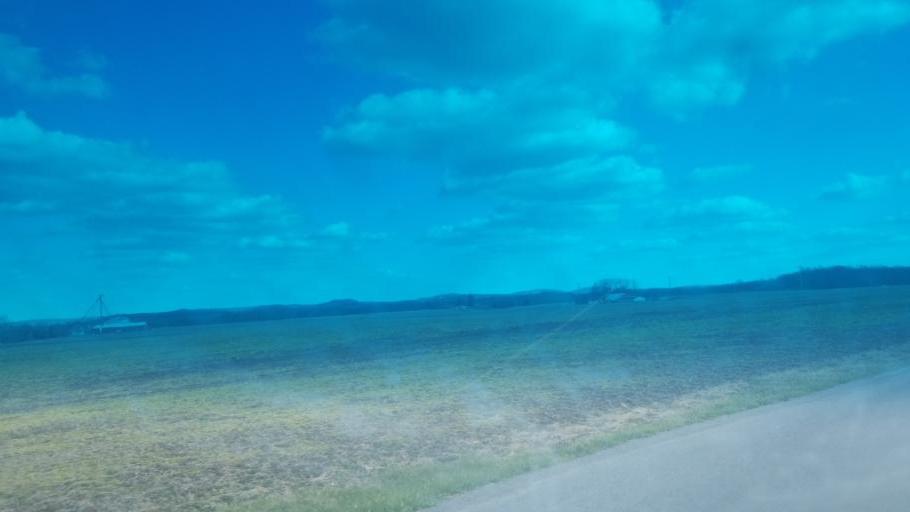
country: US
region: Ohio
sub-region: Highland County
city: Greenfield
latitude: 39.3346
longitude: -83.4102
